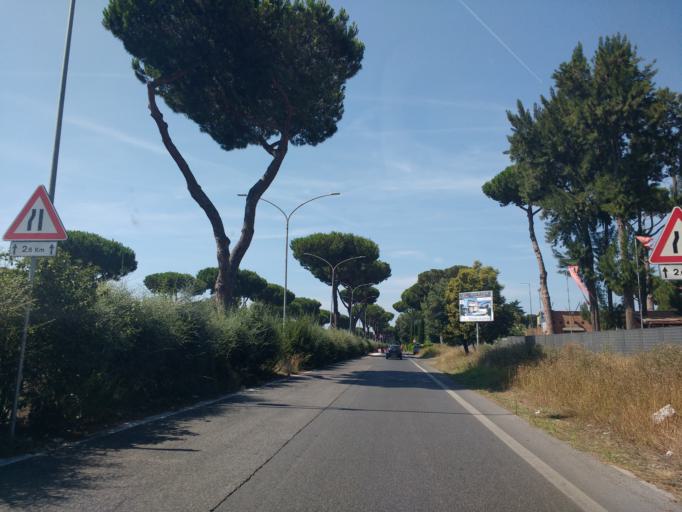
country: IT
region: Latium
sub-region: Citta metropolitana di Roma Capitale
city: Acilia-Castel Fusano-Ostia Antica
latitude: 41.7454
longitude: 12.3571
